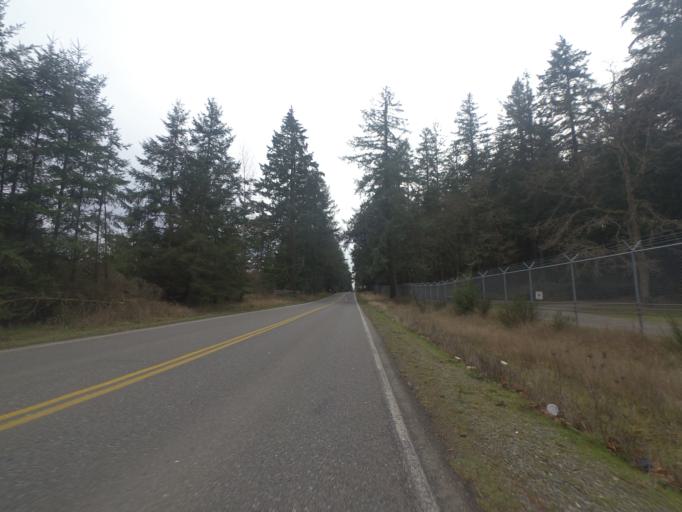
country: US
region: Washington
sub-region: Pierce County
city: McChord Air Force Base
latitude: 47.1214
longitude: -122.5126
